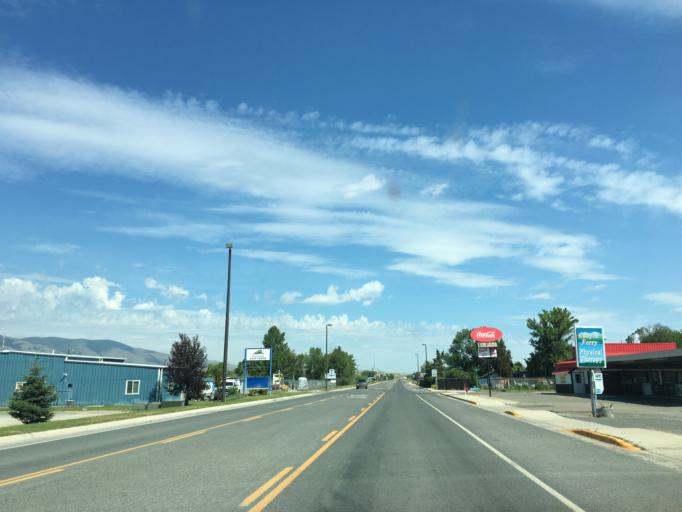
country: US
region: Montana
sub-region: Broadwater County
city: Townsend
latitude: 46.3243
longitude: -111.5248
